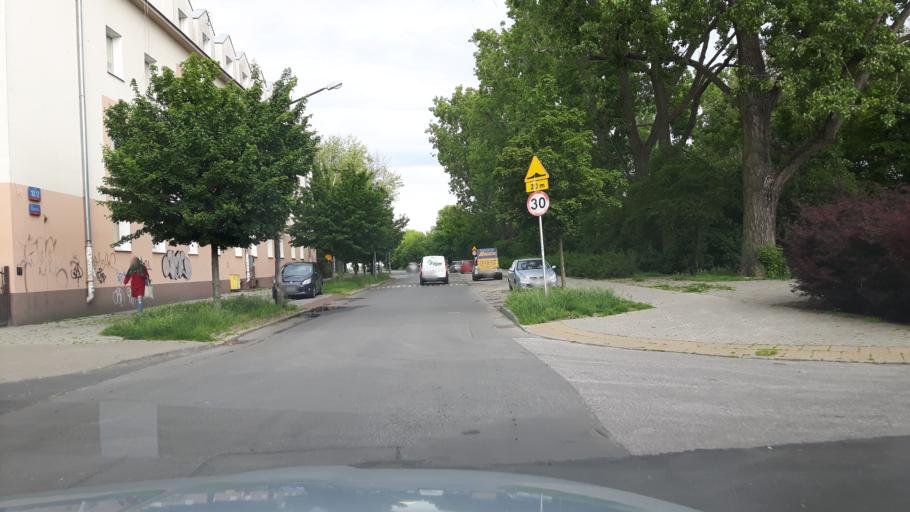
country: PL
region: Masovian Voivodeship
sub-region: Warszawa
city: Praga Poludnie
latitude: 52.2437
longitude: 21.1108
